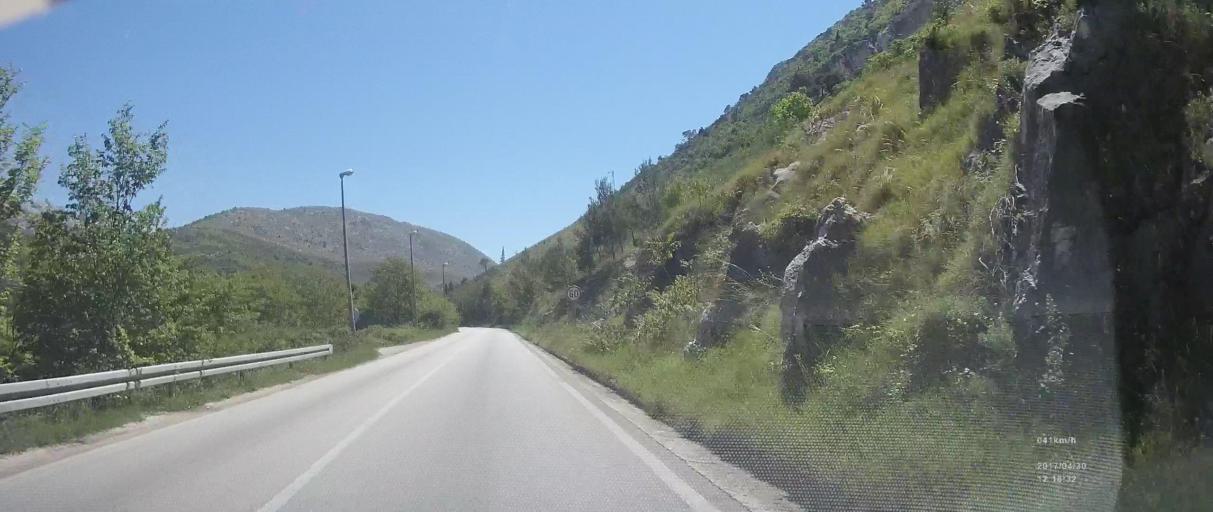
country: HR
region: Splitsko-Dalmatinska
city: Zrnovnica
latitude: 43.5190
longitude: 16.5471
